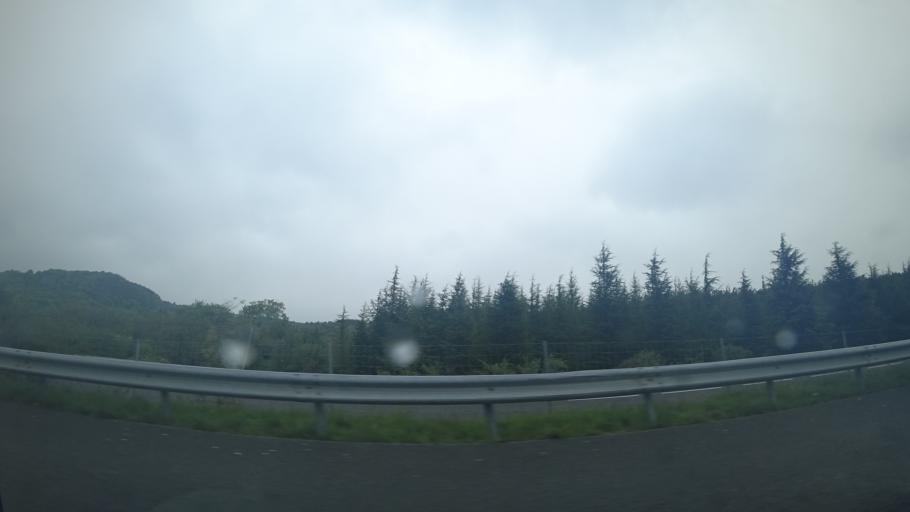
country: FR
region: Languedoc-Roussillon
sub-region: Departement de l'Herault
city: Lodeve
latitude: 43.8877
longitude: 3.2935
